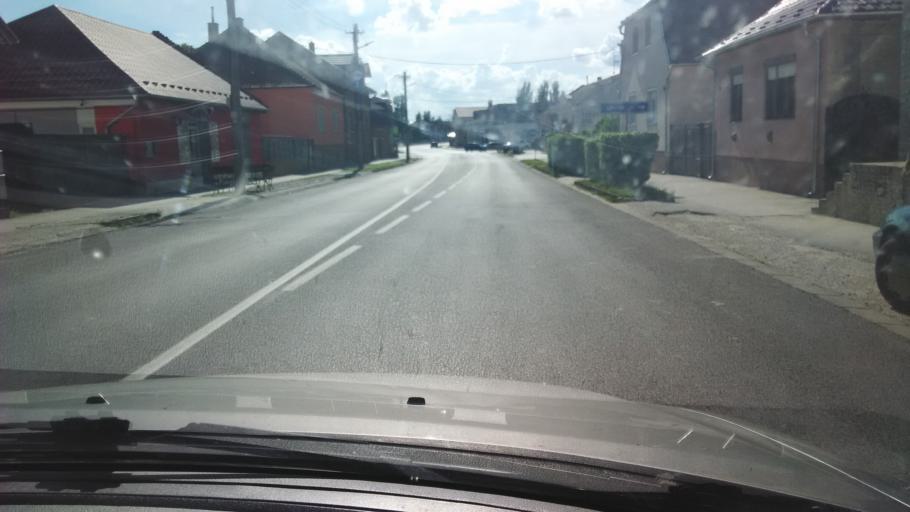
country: SK
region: Nitriansky
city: Surany
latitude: 48.0889
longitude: 18.1865
